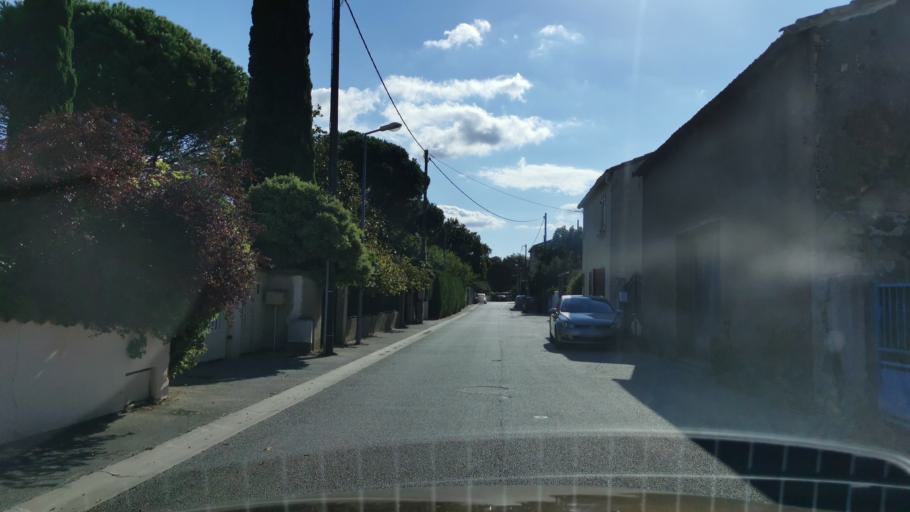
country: FR
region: Languedoc-Roussillon
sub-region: Departement de l'Aude
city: Canet
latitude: 43.2296
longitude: 2.8443
